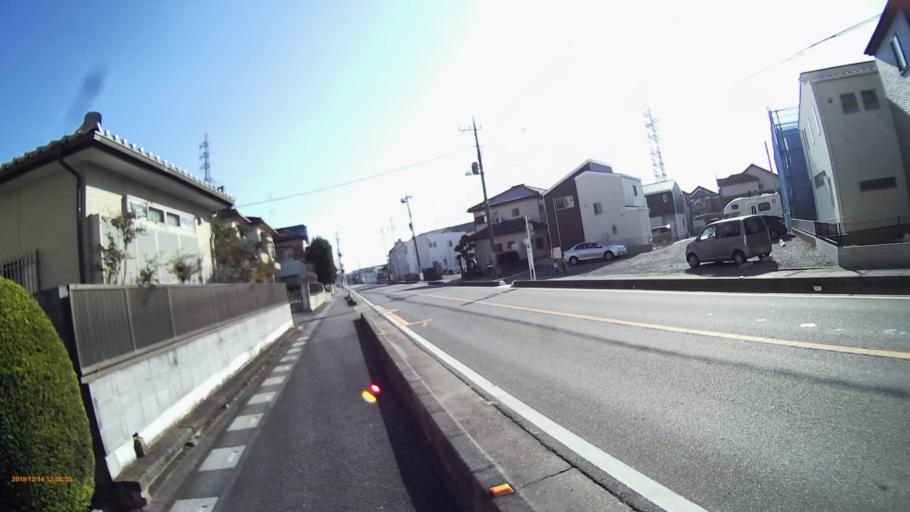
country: JP
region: Saitama
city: Fukiage-fujimi
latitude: 36.0967
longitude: 139.4621
